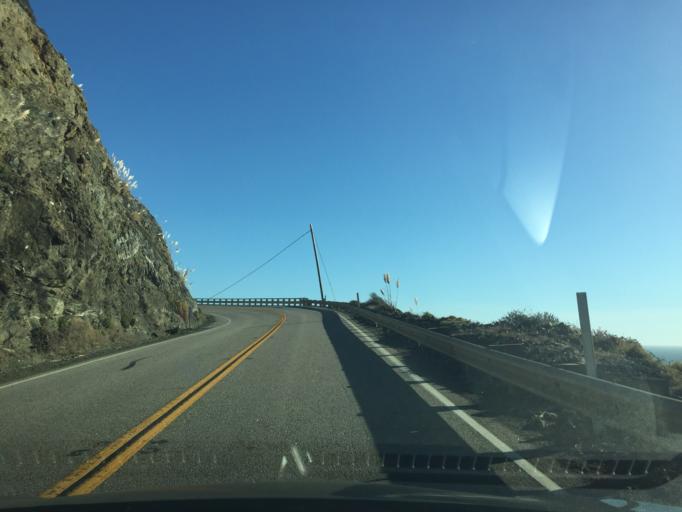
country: US
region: California
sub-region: San Luis Obispo County
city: Cambria
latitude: 35.8474
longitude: -121.4071
